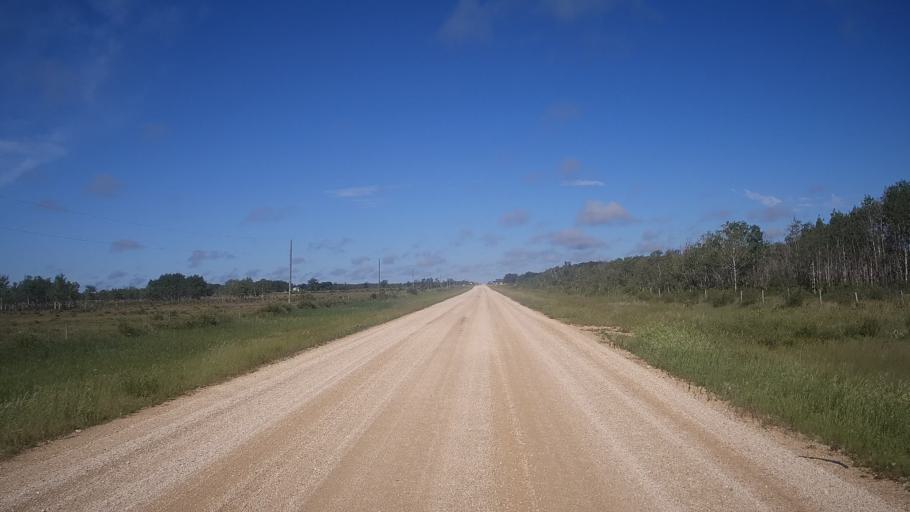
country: CA
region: Manitoba
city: Stonewall
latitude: 50.2411
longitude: -97.7260
